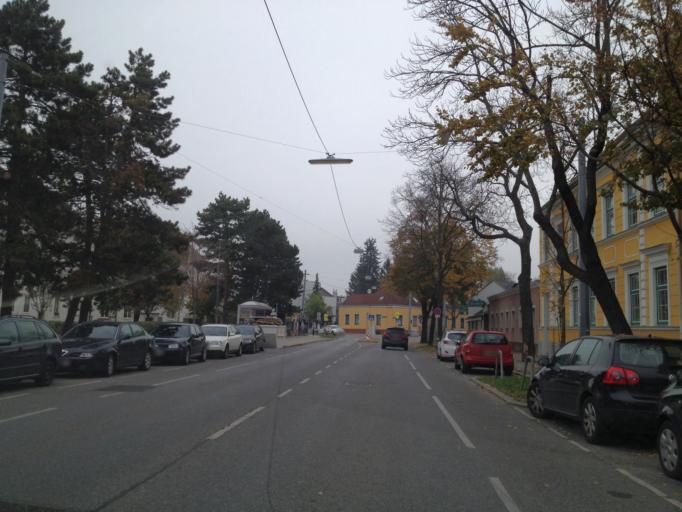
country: AT
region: Lower Austria
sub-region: Politischer Bezirk Korneuburg
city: Langenzersdorf
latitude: 48.2653
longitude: 16.3856
